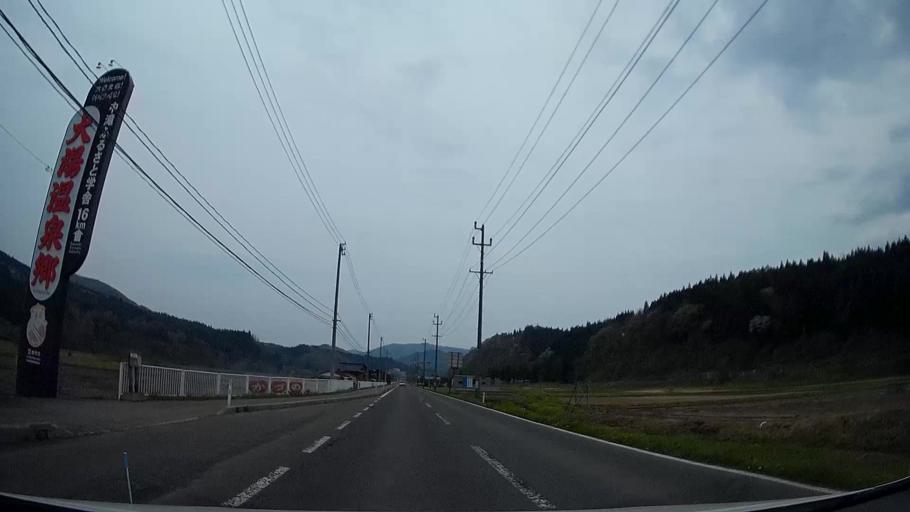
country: JP
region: Akita
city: Hanawa
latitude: 40.2880
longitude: 140.8093
